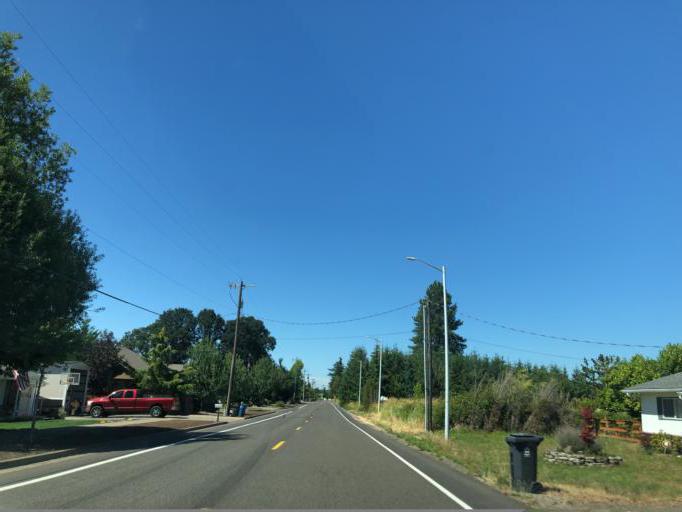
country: US
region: Oregon
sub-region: Marion County
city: Silverton
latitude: 45.0172
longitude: -122.7688
